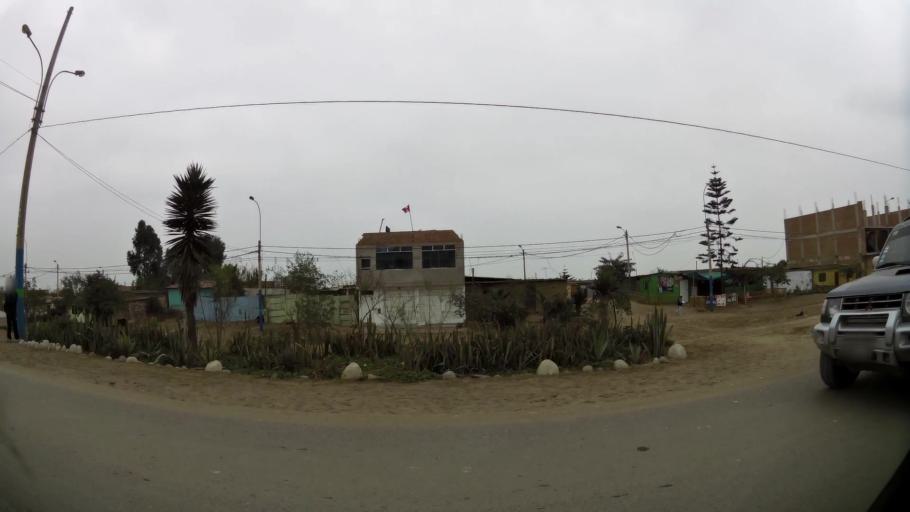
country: PE
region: Lima
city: Ventanilla
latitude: -11.8466
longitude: -77.1385
